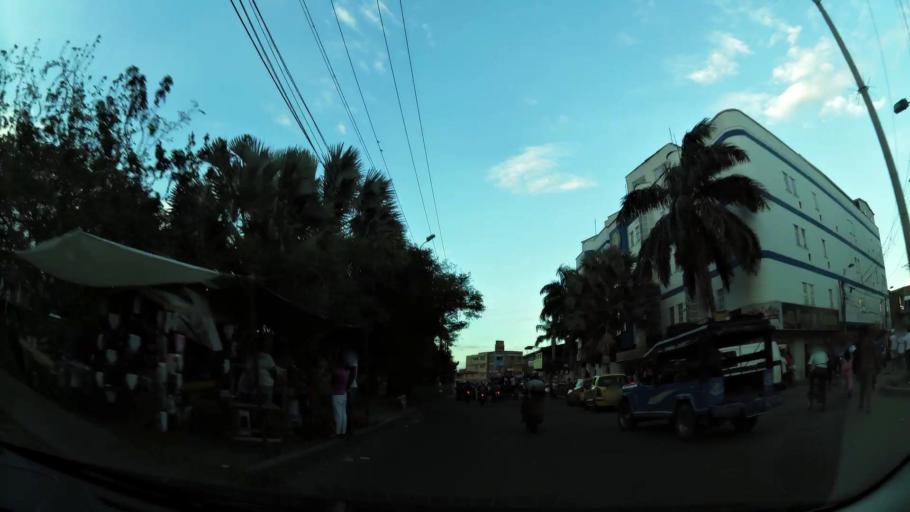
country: CO
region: Valle del Cauca
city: Cali
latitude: 3.4270
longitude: -76.4841
